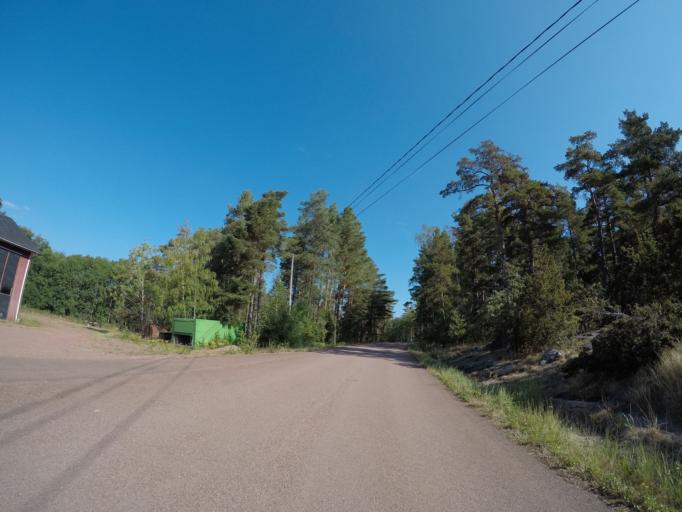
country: AX
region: Alands landsbygd
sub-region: Finstroem
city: Finstroem
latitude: 60.3308
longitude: 19.9112
